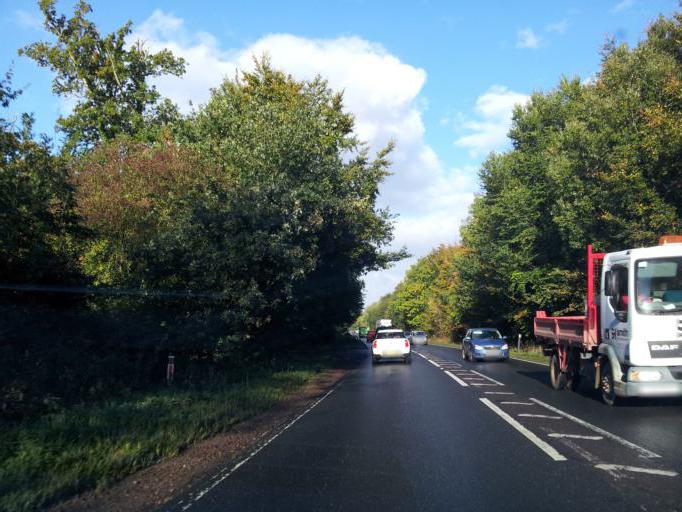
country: GB
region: England
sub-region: Norfolk
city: Mattishall
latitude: 52.6638
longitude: 1.1118
